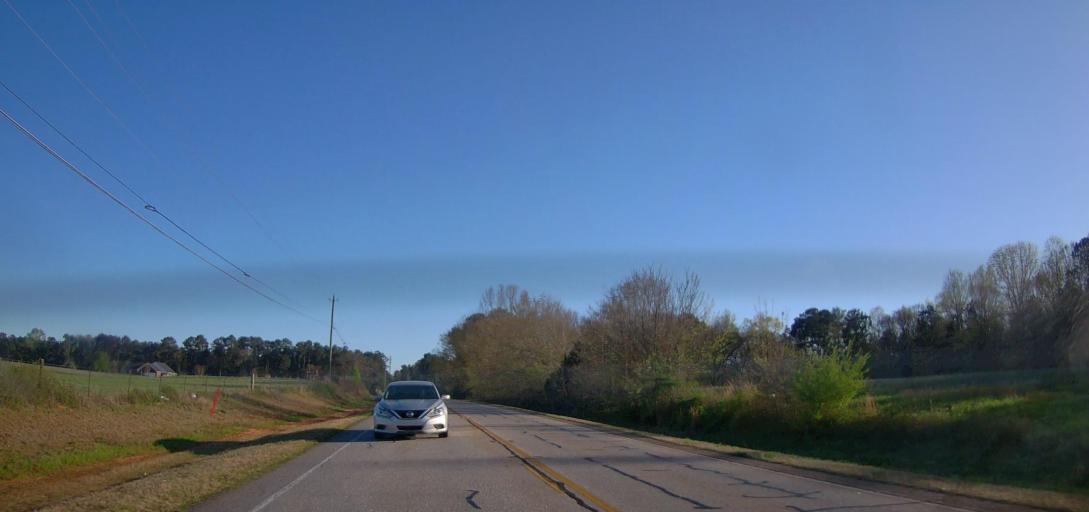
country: US
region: Georgia
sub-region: Newton County
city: Oakwood
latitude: 33.4514
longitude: -83.9036
